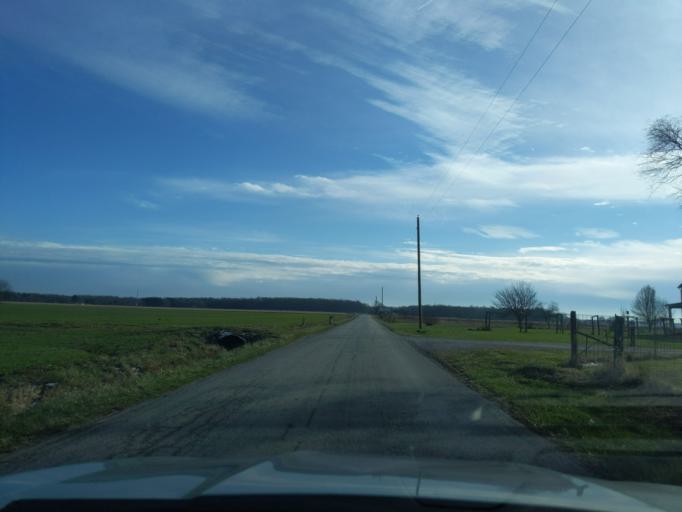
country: US
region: Indiana
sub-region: Decatur County
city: Westport
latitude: 39.1996
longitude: -85.4627
